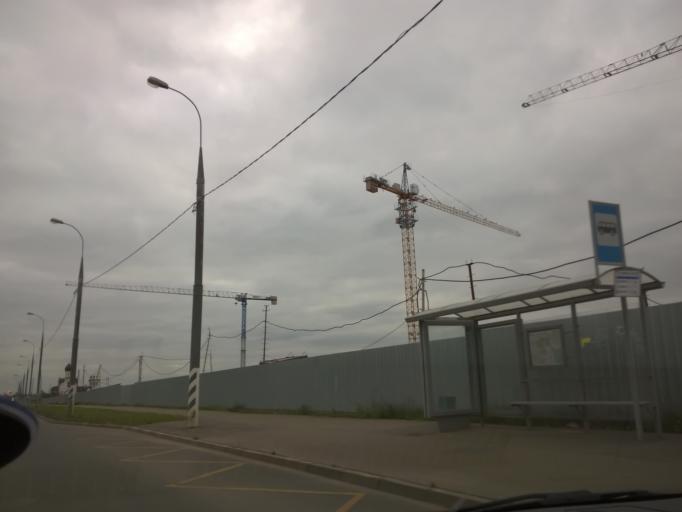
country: RU
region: Moskovskaya
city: Kommunarka
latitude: 55.5357
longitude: 37.4992
